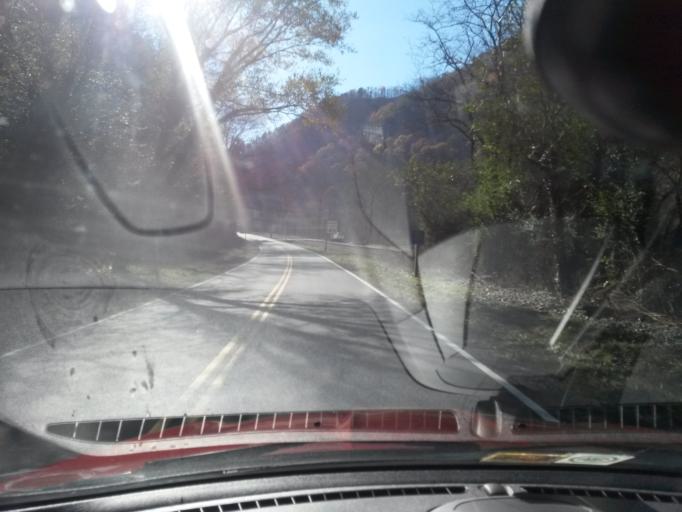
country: US
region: Virginia
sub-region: Botetourt County
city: Fincastle
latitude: 37.6471
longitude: -79.8086
